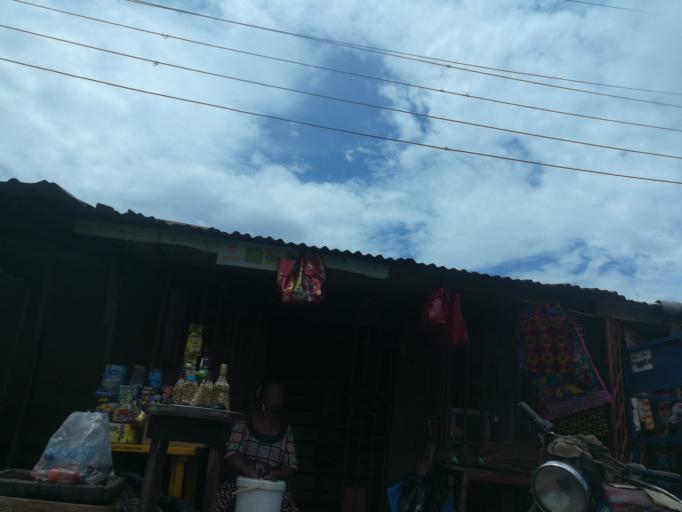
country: NG
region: Lagos
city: Agege
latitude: 6.6197
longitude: 3.3310
